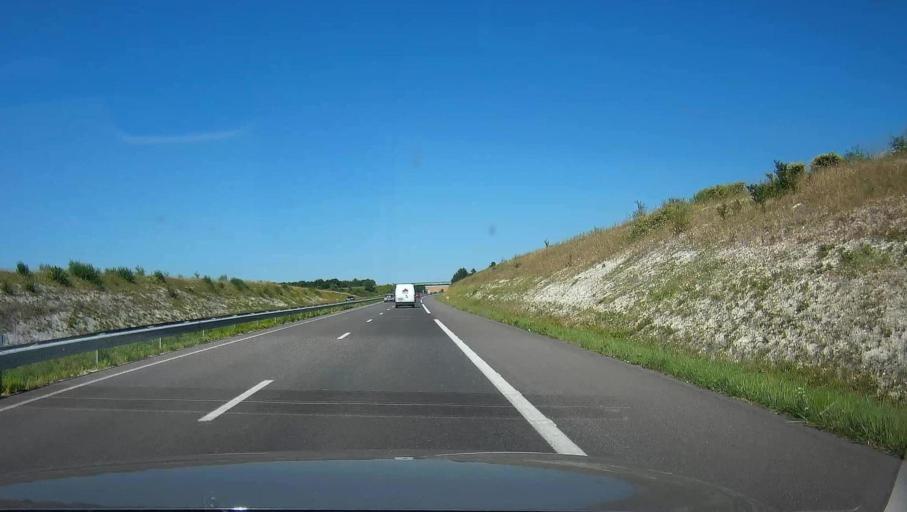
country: FR
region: Champagne-Ardenne
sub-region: Departement de la Marne
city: Fagnieres
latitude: 49.0284
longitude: 4.2854
